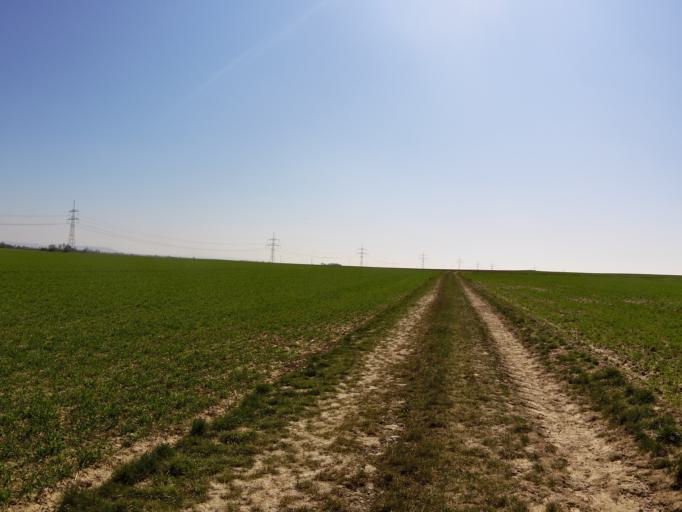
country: DE
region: Bavaria
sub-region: Regierungsbezirk Unterfranken
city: Oberpleichfeld
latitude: 49.8394
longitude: 10.0832
